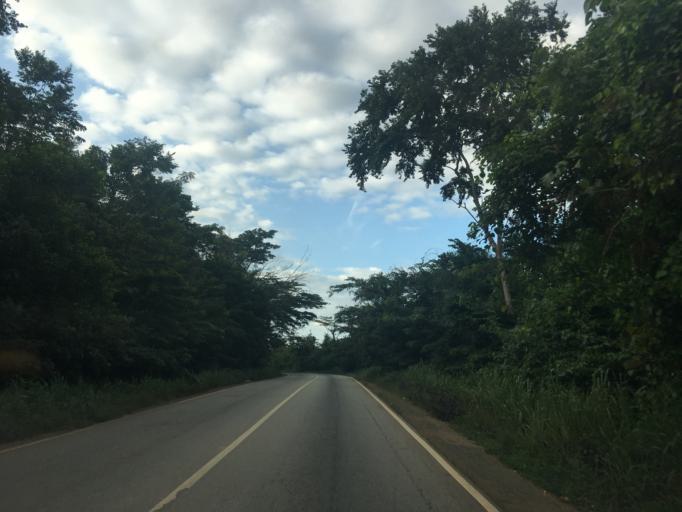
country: GH
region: Western
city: Bibiani
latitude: 6.4166
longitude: -2.3023
